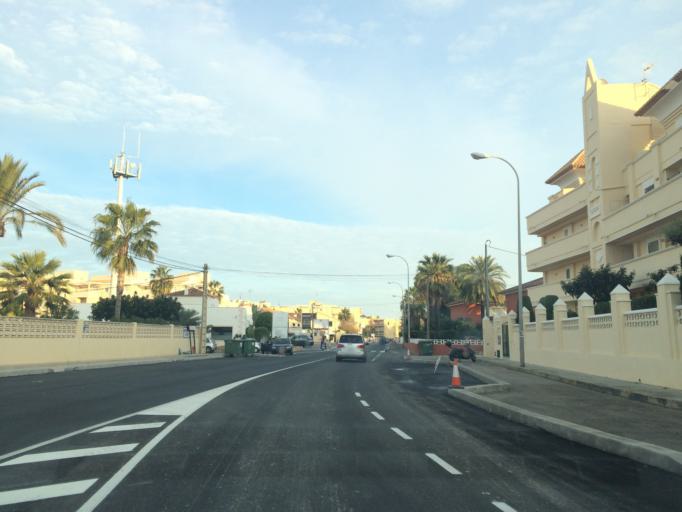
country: ES
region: Valencia
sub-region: Provincia de Alicante
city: els Poblets
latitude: 38.8585
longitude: 0.0613
